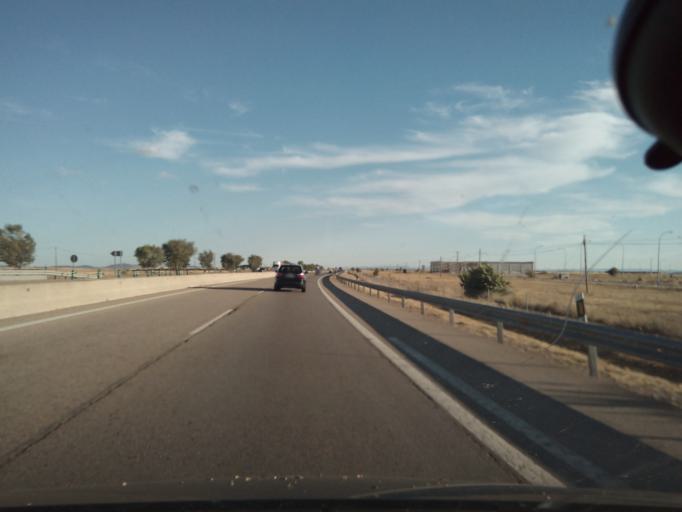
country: ES
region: Castille-La Mancha
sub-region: Province of Toledo
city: Tembleque
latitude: 39.7764
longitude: -3.4791
